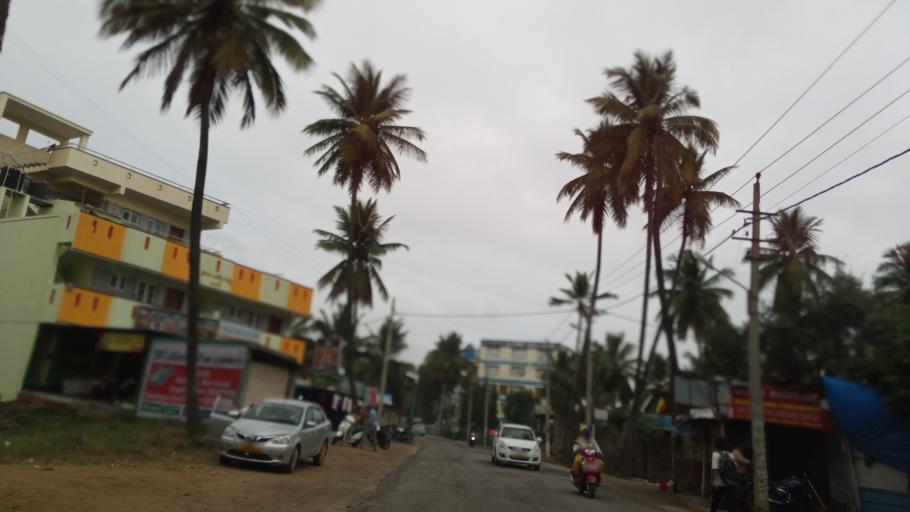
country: IN
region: Karnataka
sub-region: Bangalore Urban
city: Bangalore
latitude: 12.9105
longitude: 77.4866
